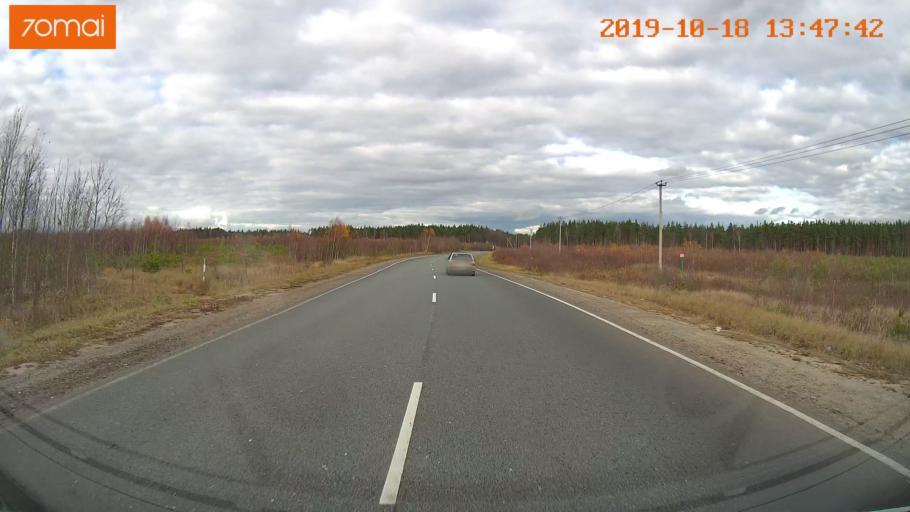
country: RU
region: Moskovskaya
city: Radovitskiy
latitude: 54.9788
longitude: 39.9515
